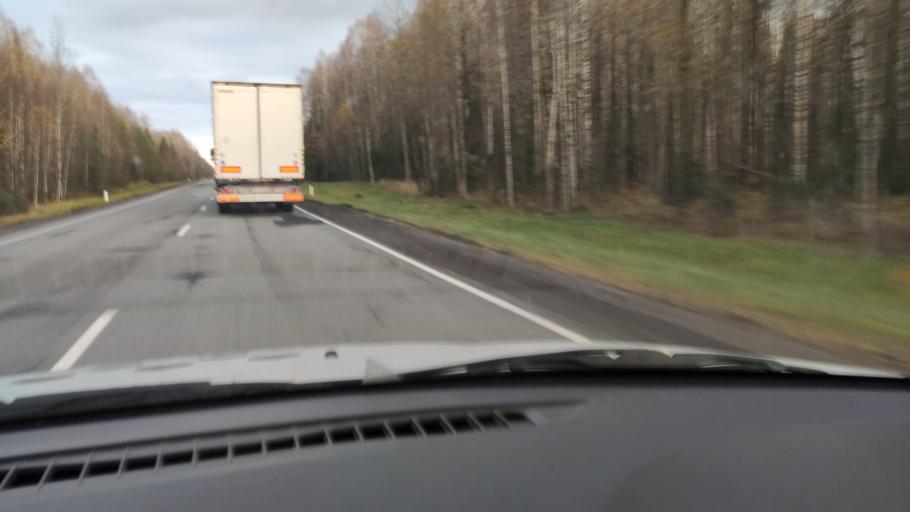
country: RU
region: Kirov
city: Chernaya Kholunitsa
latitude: 58.7719
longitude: 51.9491
